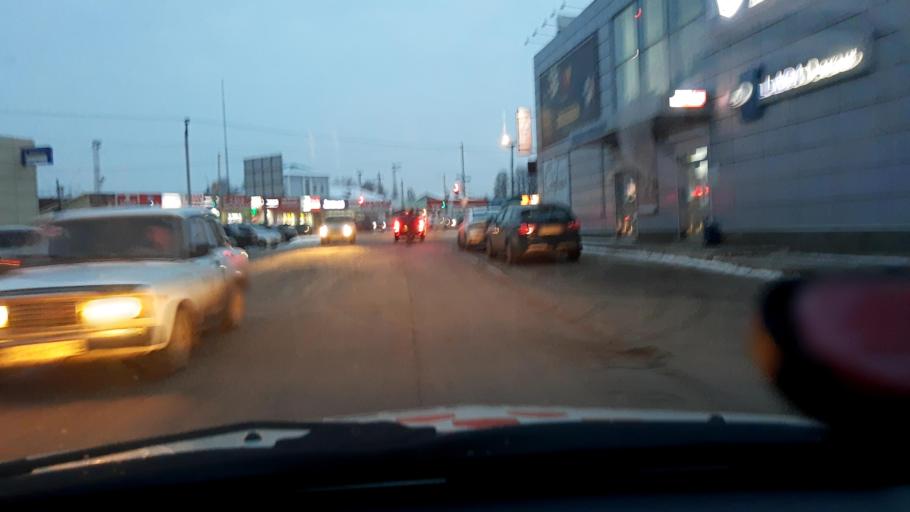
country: RU
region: Bashkortostan
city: Iglino
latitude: 54.8271
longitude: 56.4042
